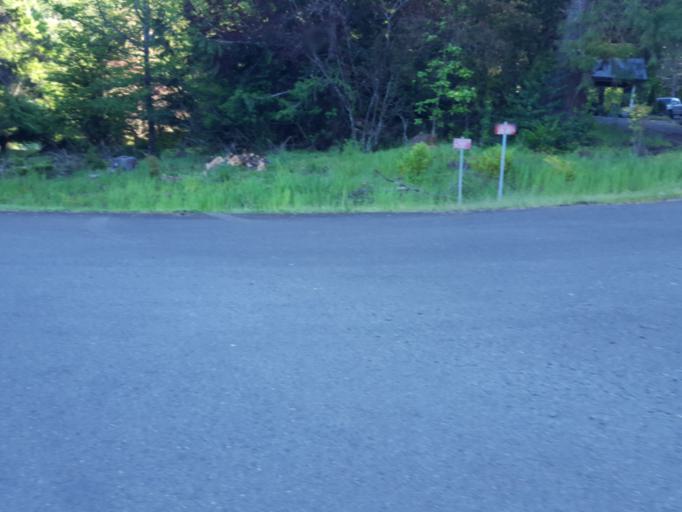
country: US
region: Oregon
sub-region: Yamhill County
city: McMinnville
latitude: 45.2221
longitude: -123.2695
